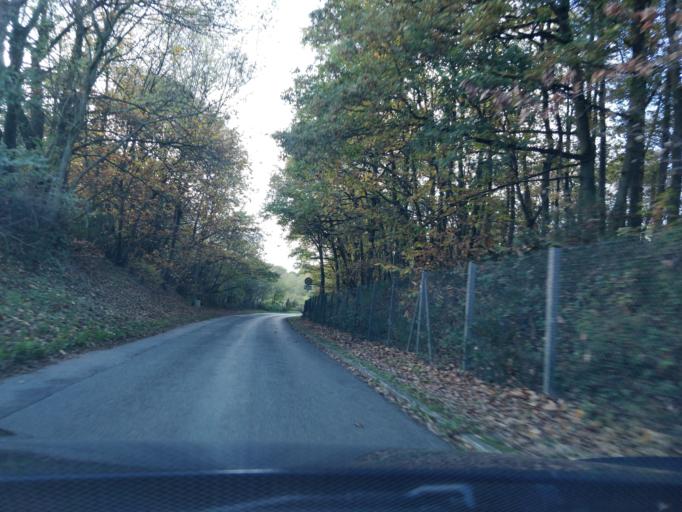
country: FR
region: Ile-de-France
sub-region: Departement de l'Essonne
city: Briis-sous-Forges
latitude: 48.6282
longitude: 2.1345
